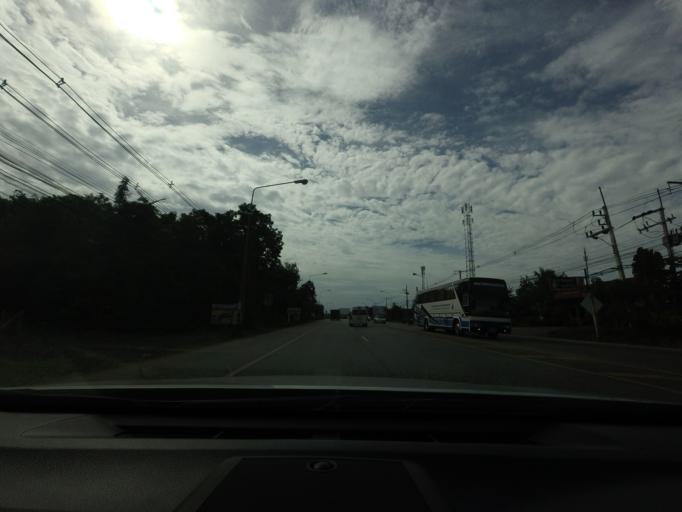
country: TH
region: Songkhla
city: Hat Yai
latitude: 6.9734
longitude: 100.4285
